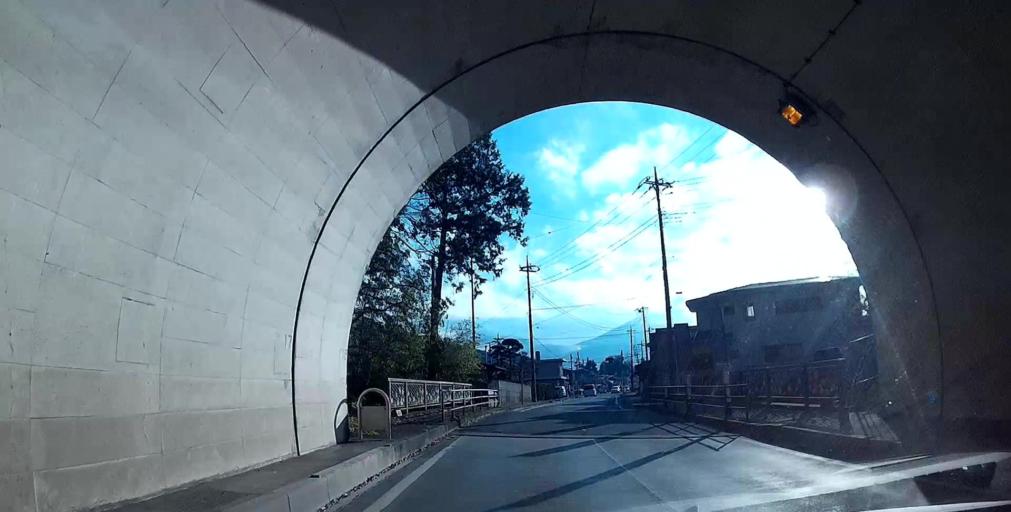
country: JP
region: Yamanashi
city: Fujikawaguchiko
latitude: 35.4891
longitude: 138.8211
